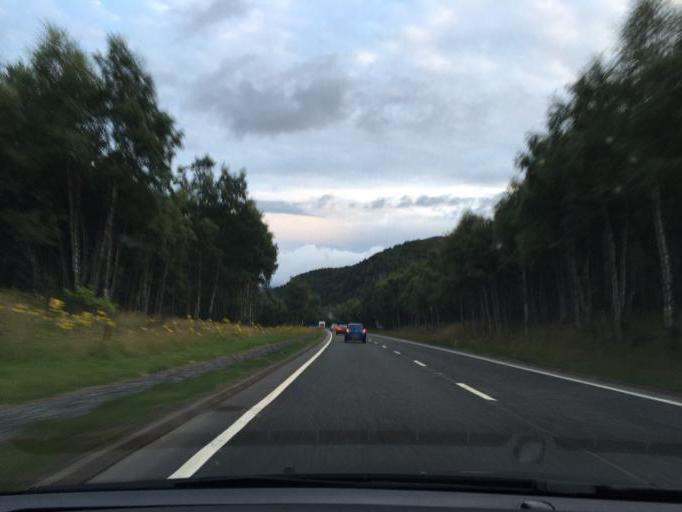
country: GB
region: Scotland
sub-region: Highland
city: Aviemore
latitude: 57.1939
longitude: -3.8367
